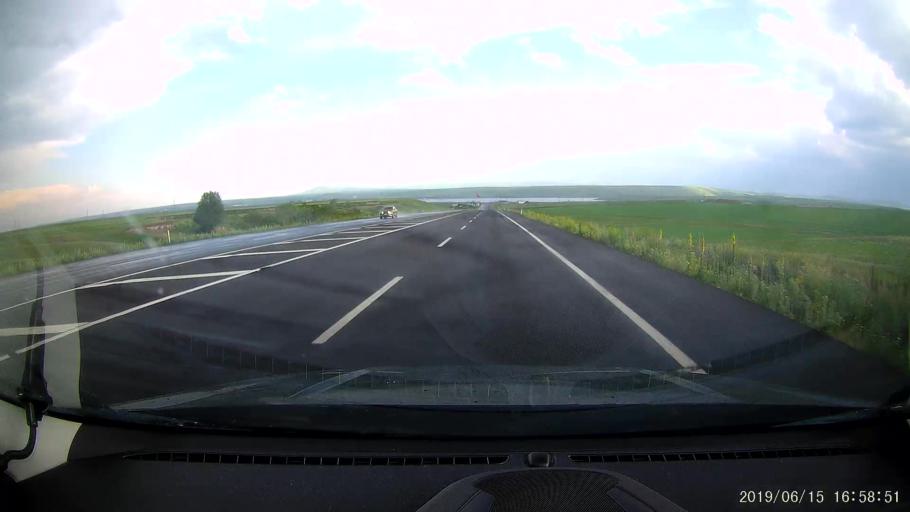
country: TR
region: Kars
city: Susuz
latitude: 40.7594
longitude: 43.1465
